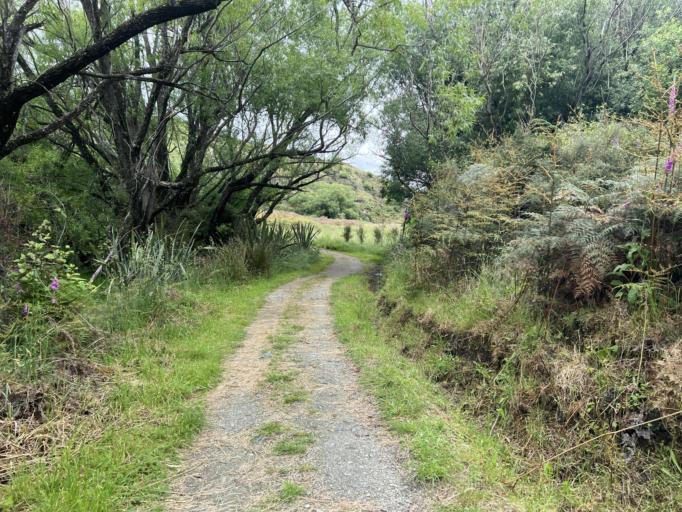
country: NZ
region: Otago
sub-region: Queenstown-Lakes District
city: Wanaka
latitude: -44.6482
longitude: 168.9624
